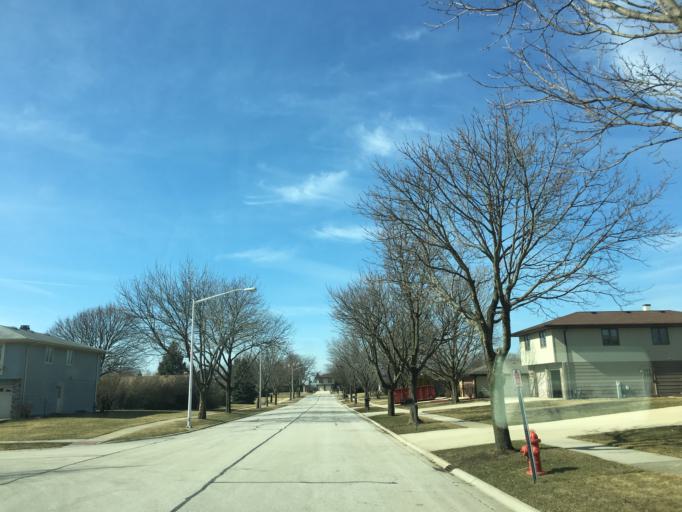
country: US
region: Illinois
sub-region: DuPage County
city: Hanover Park
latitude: 42.0238
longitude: -88.1354
